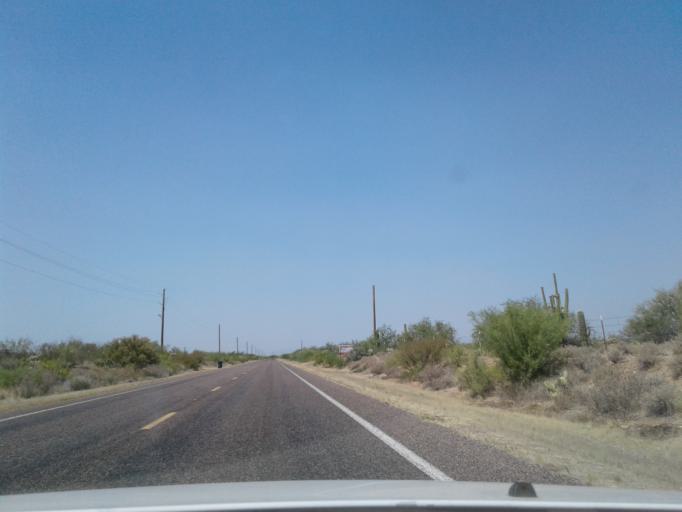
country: US
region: Arizona
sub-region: Pima County
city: Catalina
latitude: 32.6512
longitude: -111.1044
